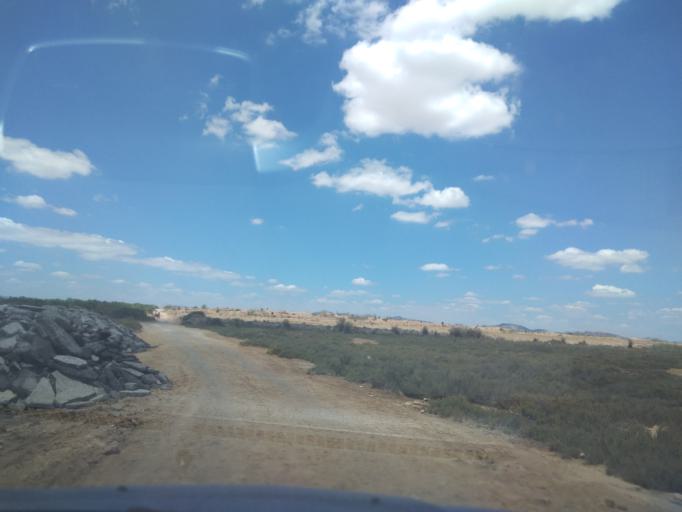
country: TN
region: Susah
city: Harqalah
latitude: 36.1645
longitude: 10.4495
